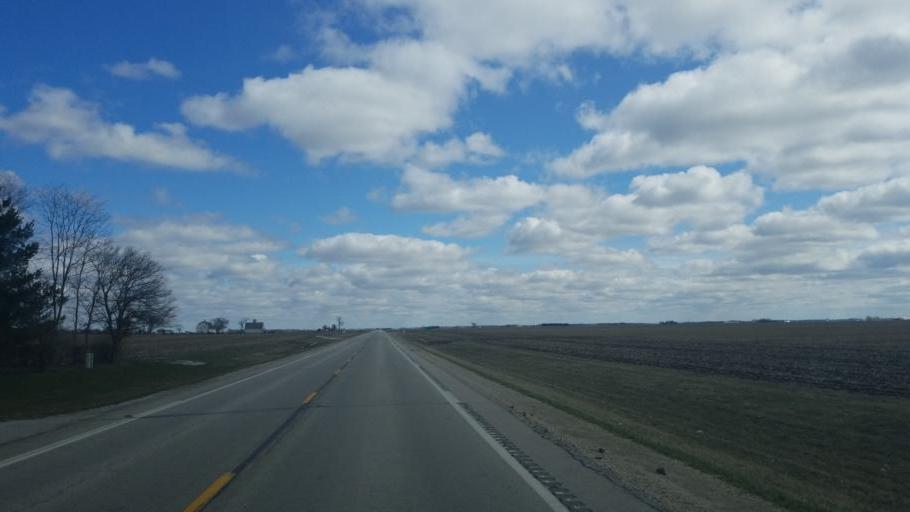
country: US
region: Illinois
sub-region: Douglas County
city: Villa Grove
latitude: 39.7918
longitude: -88.1517
